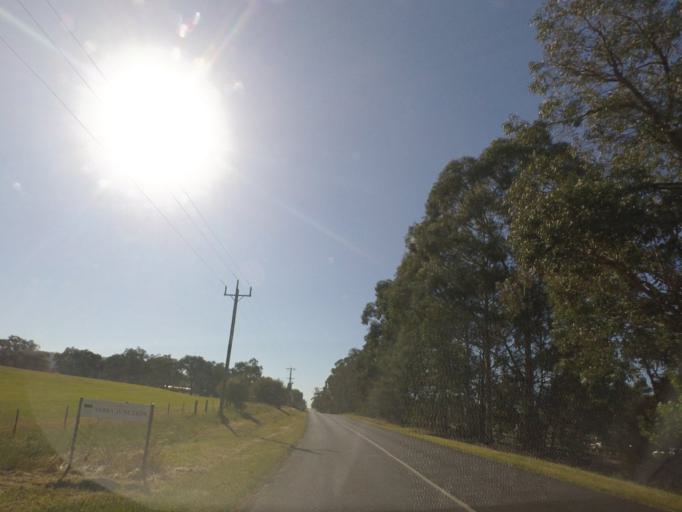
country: AU
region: Victoria
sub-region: Yarra Ranges
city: Yarra Junction
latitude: -37.7962
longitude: 145.6307
